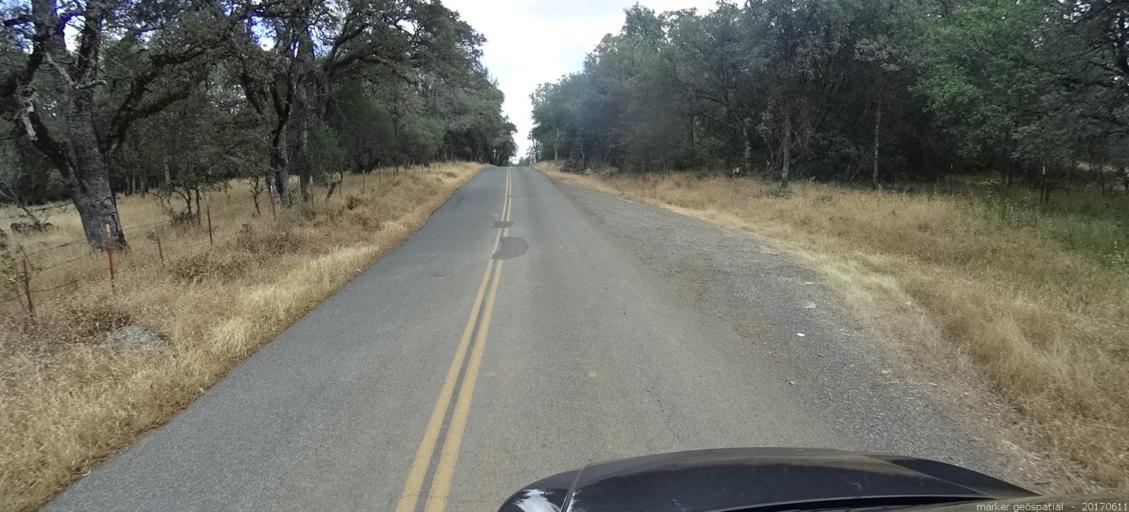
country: US
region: California
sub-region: Butte County
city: Oroville
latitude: 39.6177
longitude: -121.5265
